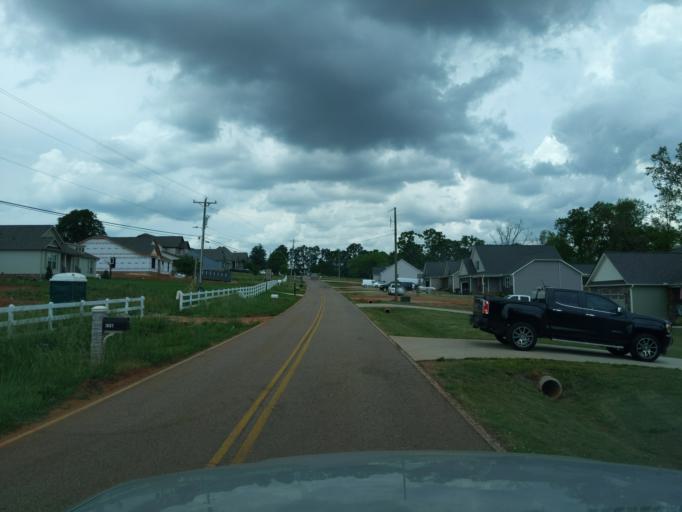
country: US
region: South Carolina
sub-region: Spartanburg County
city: Inman Mills
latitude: 35.0250
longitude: -82.1253
